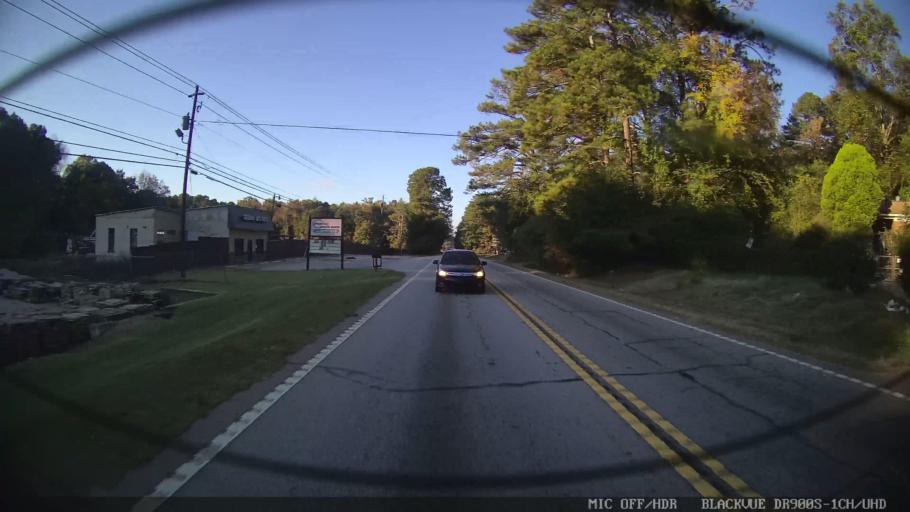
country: US
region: Georgia
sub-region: Henry County
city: Stockbridge
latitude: 33.5591
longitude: -84.2604
